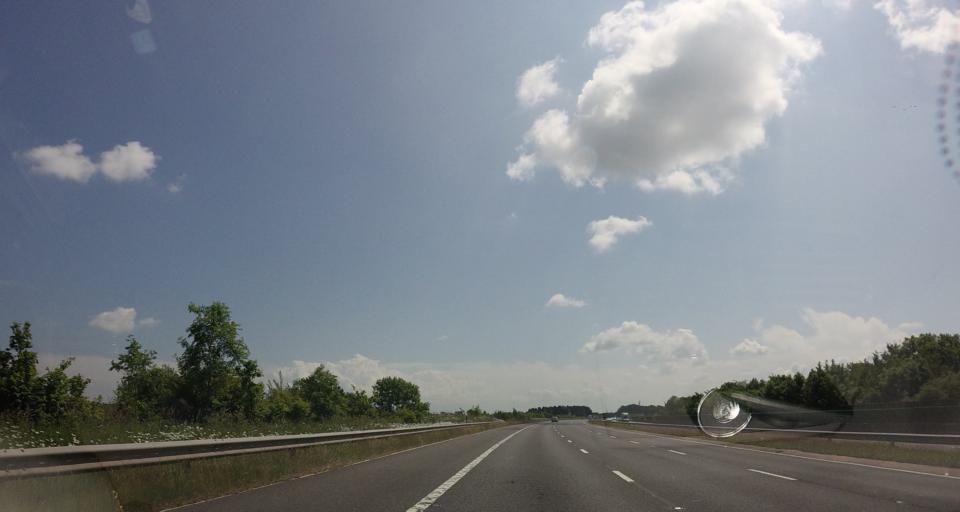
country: GB
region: Scotland
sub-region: Dumfries and Galloway
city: Gretna
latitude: 54.9738
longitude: -3.0073
